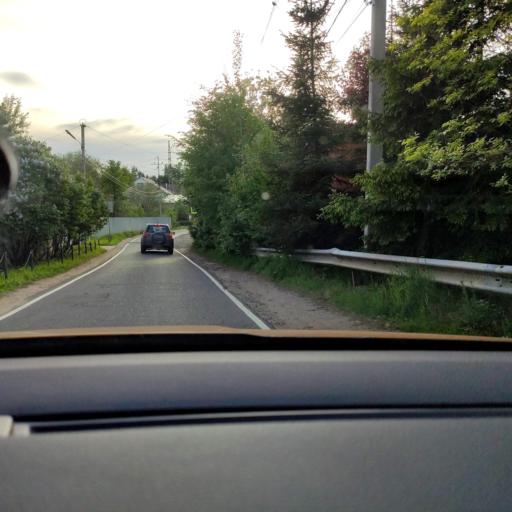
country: RU
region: Moskovskaya
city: Selyatino
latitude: 55.5267
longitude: 37.0105
